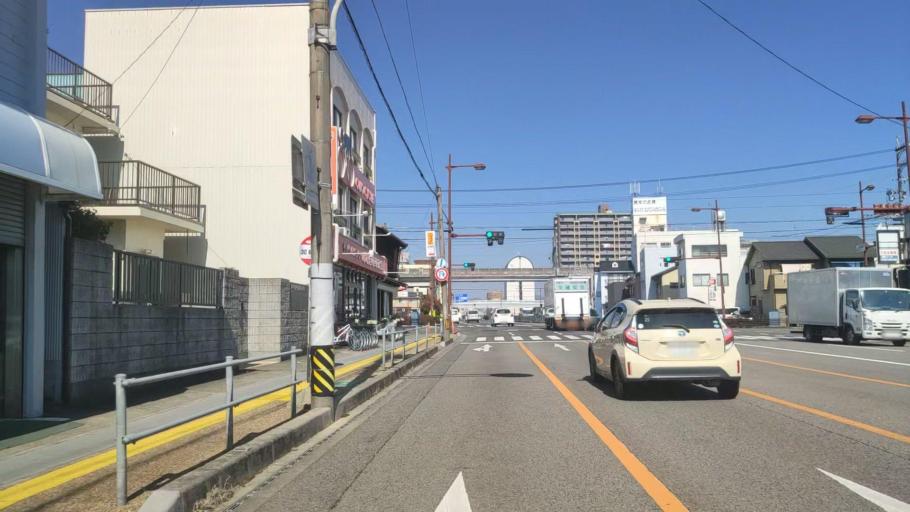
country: JP
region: Gifu
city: Gifu-shi
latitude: 35.4087
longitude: 136.7474
